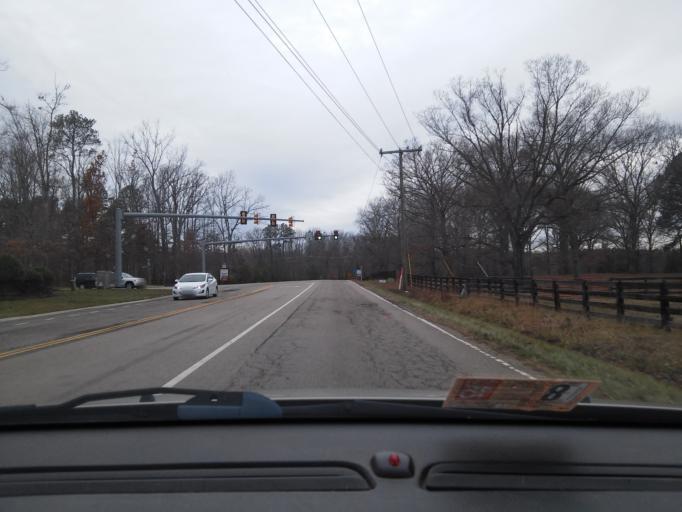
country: US
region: Virginia
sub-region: Henrico County
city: Short Pump
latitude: 37.5546
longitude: -77.6683
